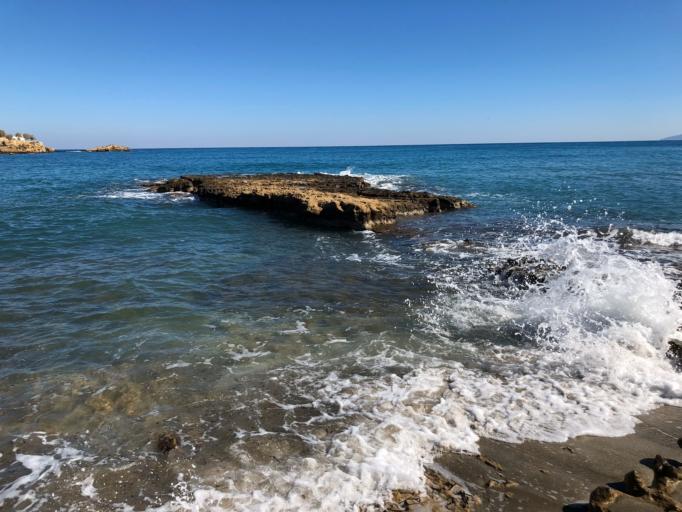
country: GR
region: Crete
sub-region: Nomos Irakleiou
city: Limin Khersonisou
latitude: 35.3340
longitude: 25.3844
